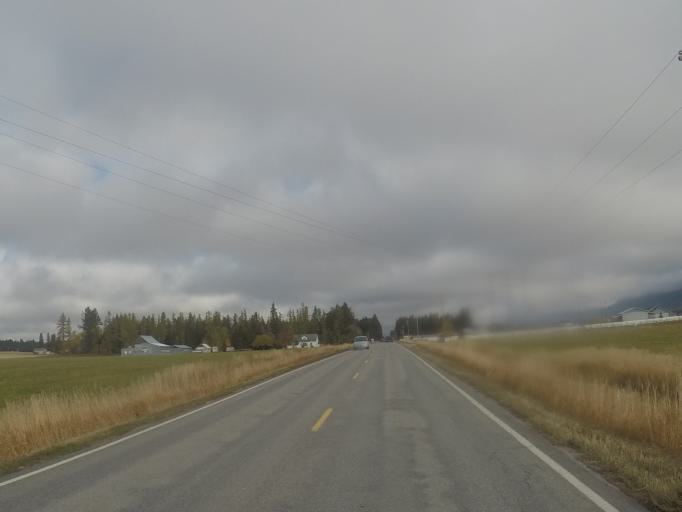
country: US
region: Montana
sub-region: Flathead County
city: Columbia Falls
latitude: 48.3069
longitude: -114.1594
